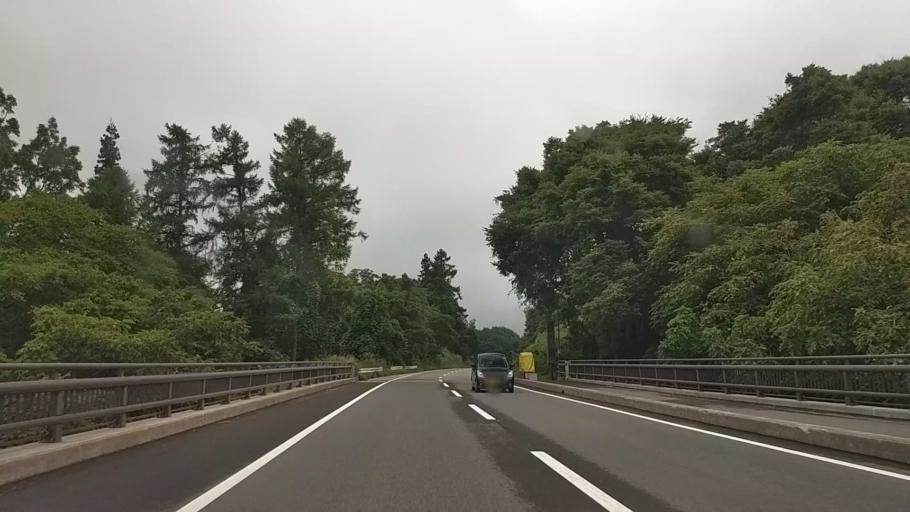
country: JP
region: Nagano
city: Iiyama
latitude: 36.8172
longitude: 138.3443
